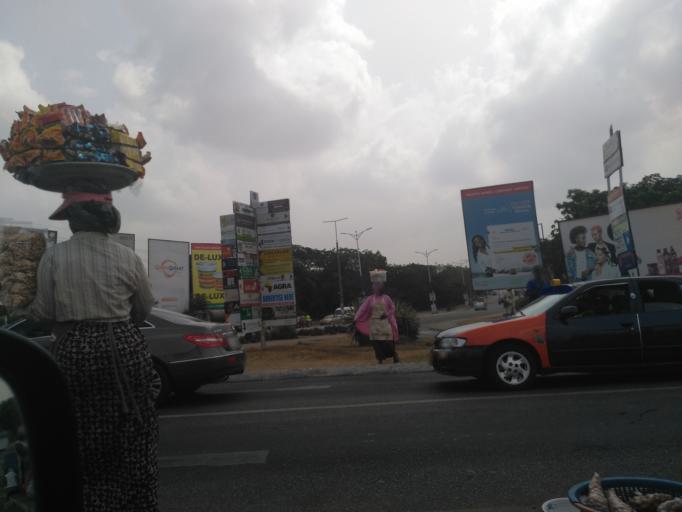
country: GH
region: Greater Accra
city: Accra
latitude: 5.5950
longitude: -0.1892
